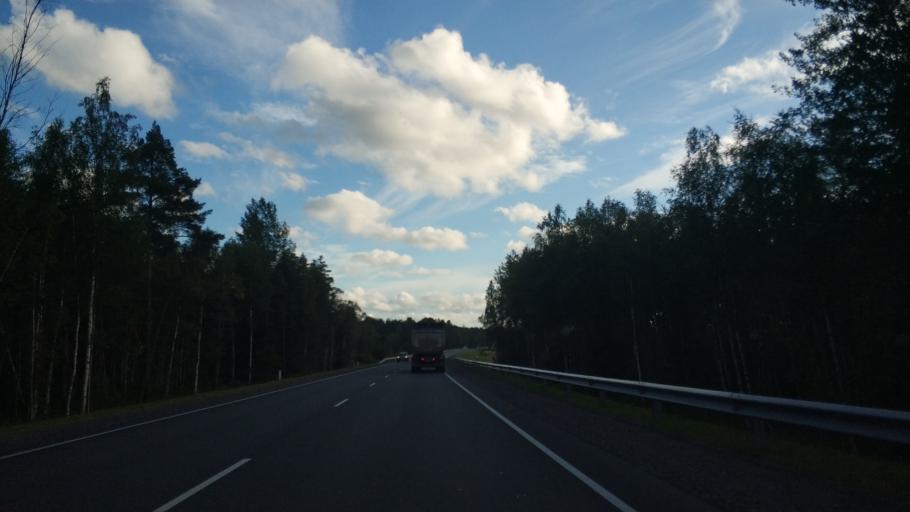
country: RU
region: Leningrad
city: Priozersk
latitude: 60.8629
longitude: 30.1585
